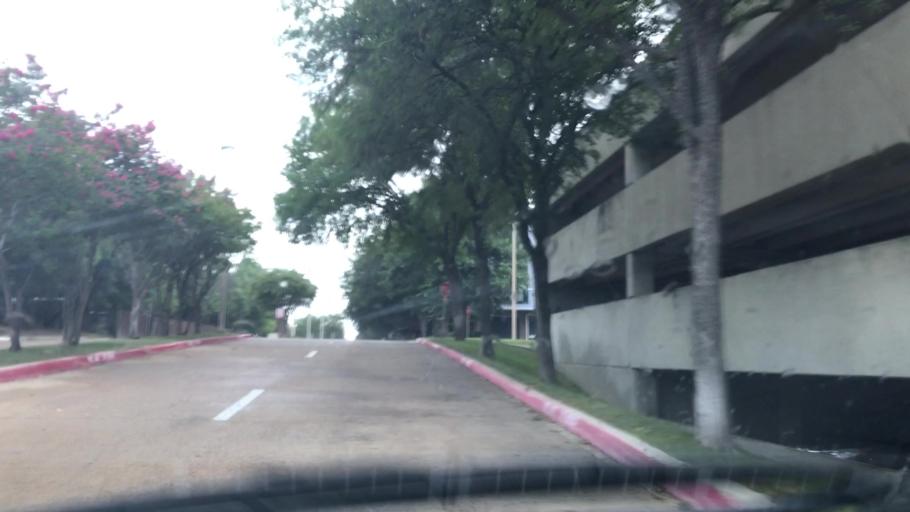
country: US
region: Texas
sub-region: Dallas County
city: Addison
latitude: 32.9493
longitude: -96.8064
